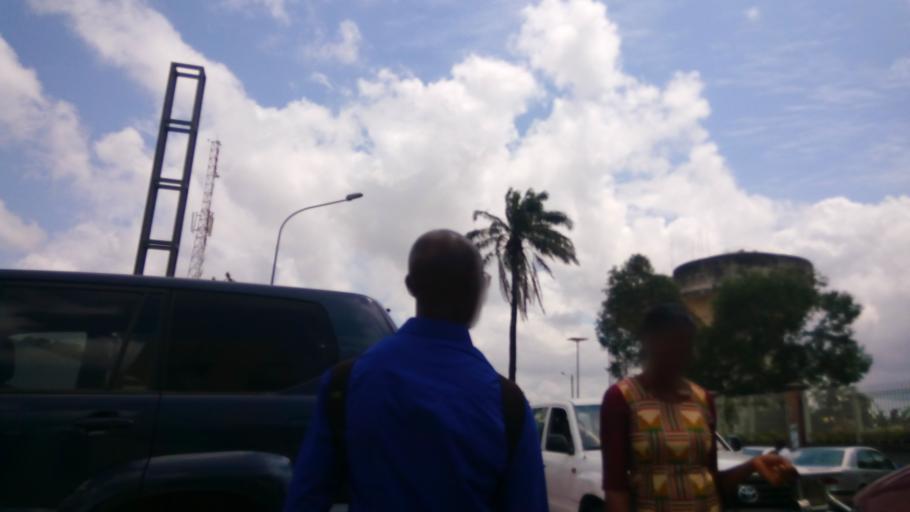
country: CI
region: Lagunes
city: Abidjan
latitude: 5.3318
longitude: -4.0231
